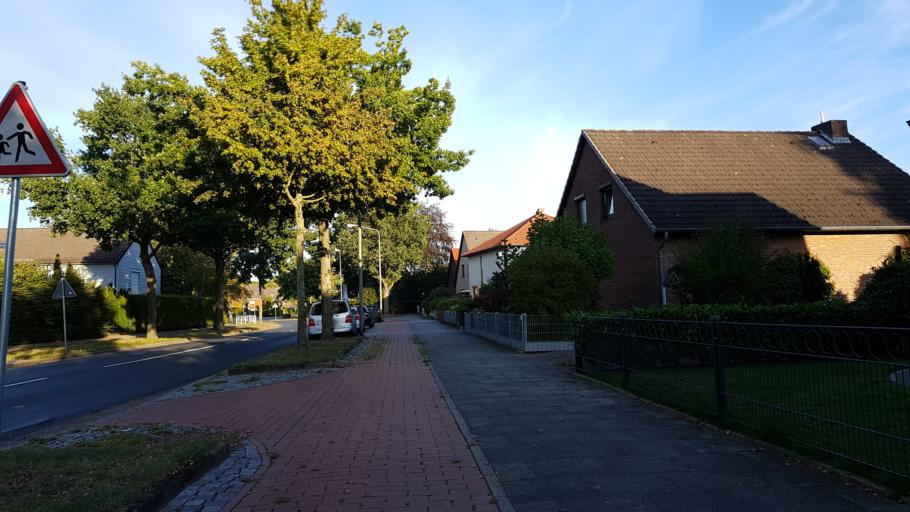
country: DE
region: Lower Saxony
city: Riede
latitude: 53.0444
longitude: 8.9191
